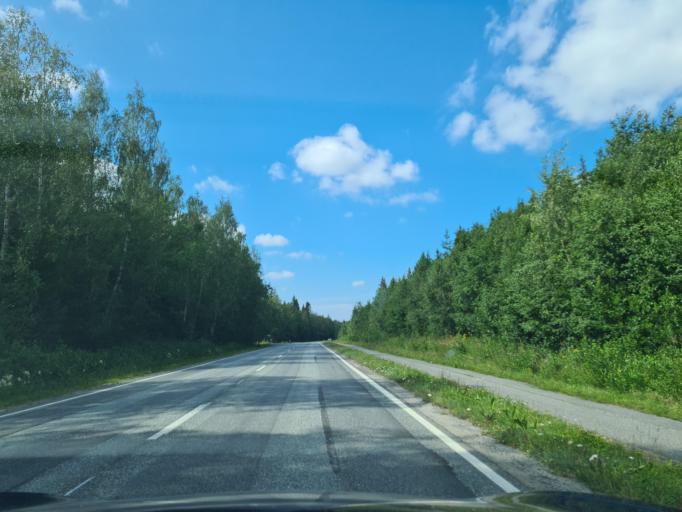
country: FI
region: Ostrobothnia
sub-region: Vaasa
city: Replot
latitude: 63.1984
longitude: 21.5391
